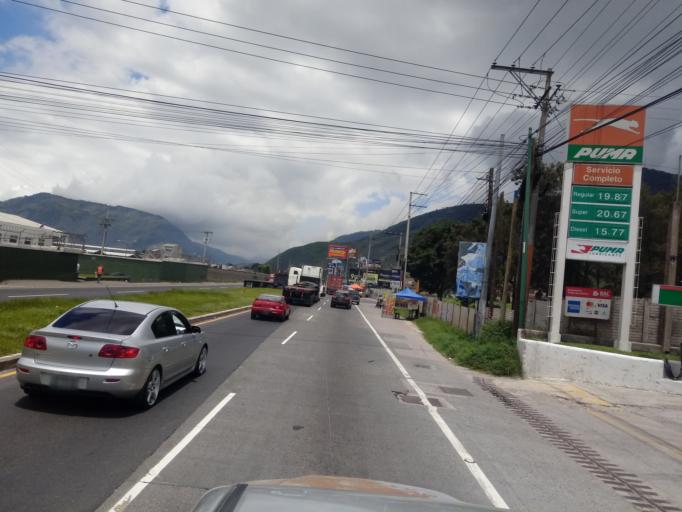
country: GT
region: Guatemala
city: Amatitlan
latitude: 14.4726
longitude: -90.6355
